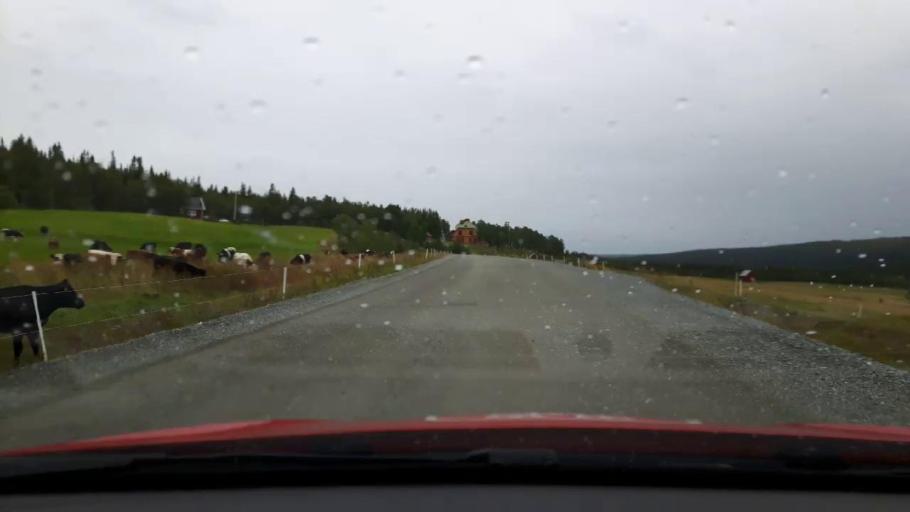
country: NO
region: Nord-Trondelag
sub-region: Meraker
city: Meraker
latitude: 63.5236
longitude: 12.4025
